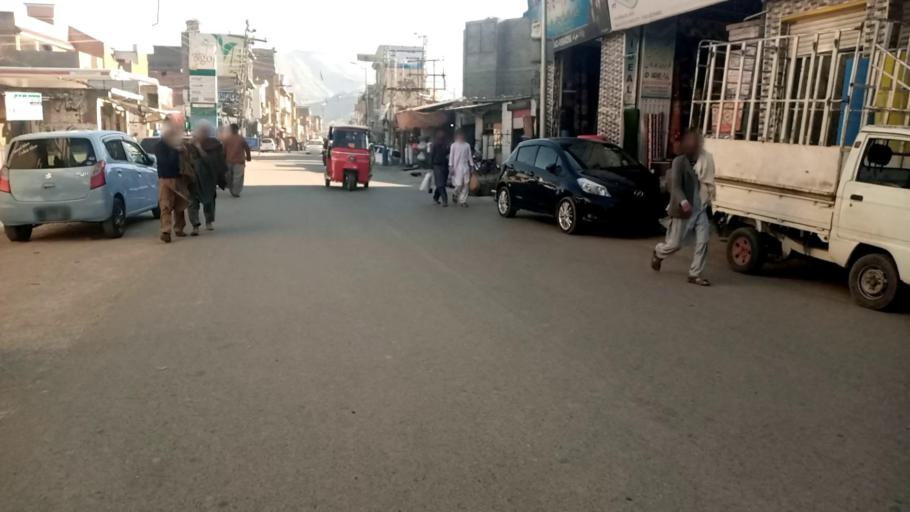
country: PK
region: Khyber Pakhtunkhwa
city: Mingora
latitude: 34.7840
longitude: 72.3537
